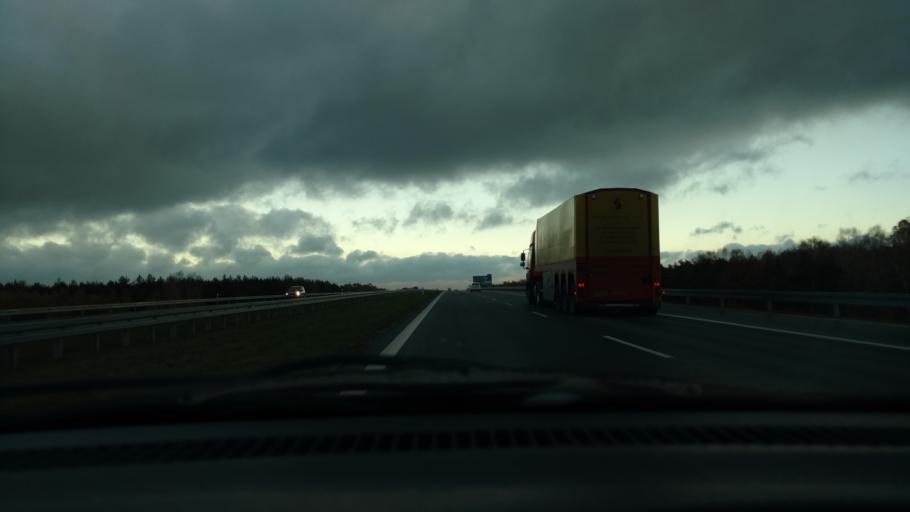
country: PL
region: Lodz Voivodeship
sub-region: Powiat lodzki wschodni
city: Andrespol
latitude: 51.7274
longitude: 19.6059
